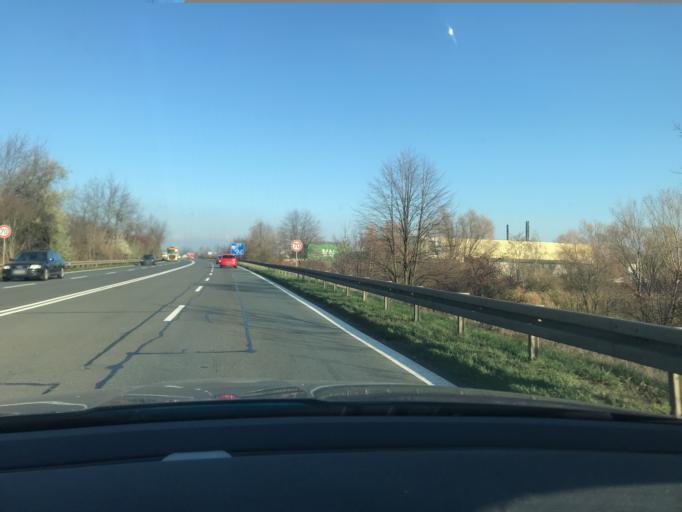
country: CZ
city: Stezery
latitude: 50.2173
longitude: 15.7876
